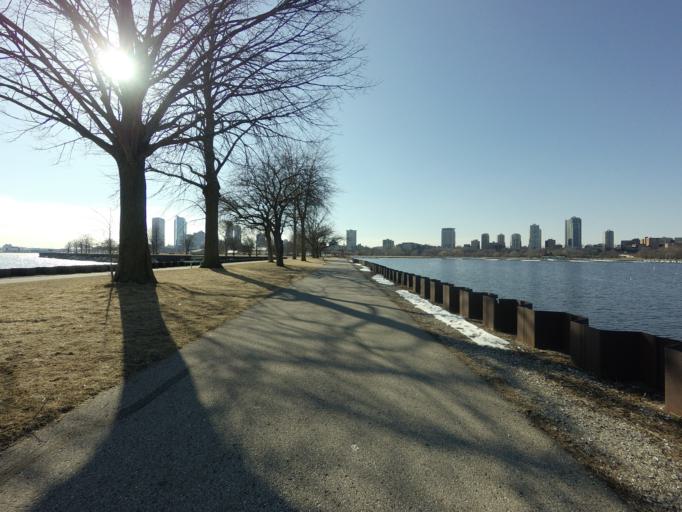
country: US
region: Wisconsin
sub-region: Milwaukee County
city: Milwaukee
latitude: 43.0463
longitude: -87.8832
